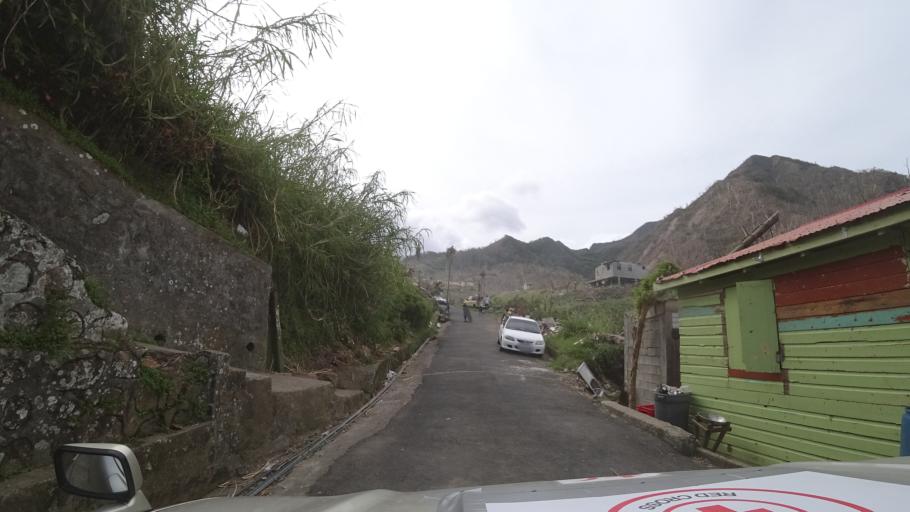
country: DM
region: Saint Patrick
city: Berekua
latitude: 15.2363
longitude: -61.3360
